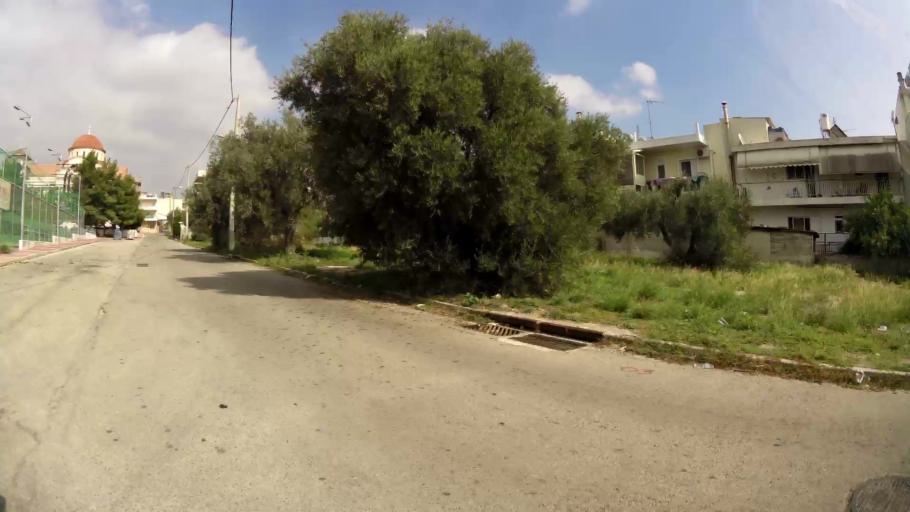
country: GR
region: Attica
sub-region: Nomarchia Dytikis Attikis
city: Zefyri
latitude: 38.0544
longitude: 23.7269
